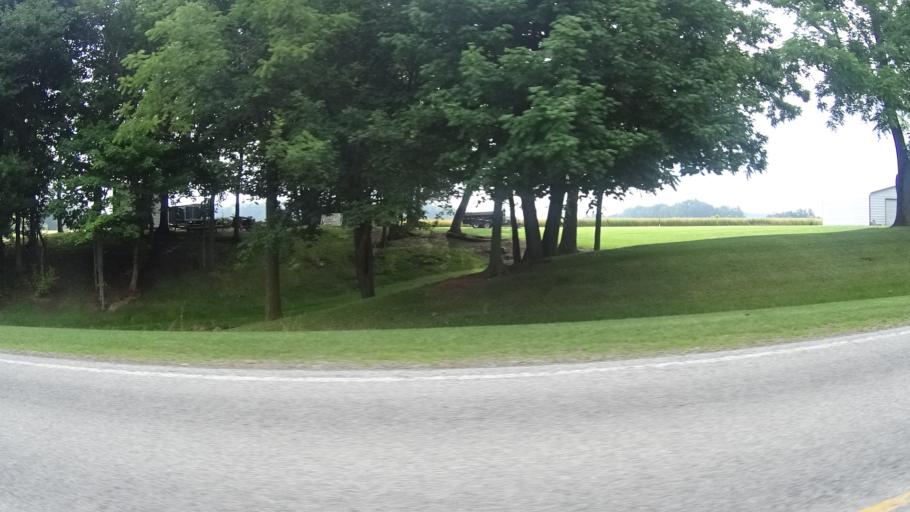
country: US
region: Ohio
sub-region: Erie County
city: Huron
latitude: 41.3472
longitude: -82.5116
